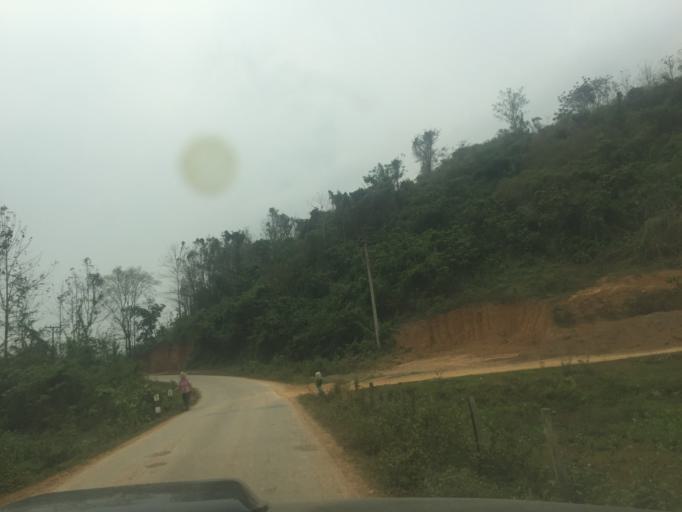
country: LA
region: Vientiane
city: Muang Sanakham
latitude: 18.3982
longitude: 101.5186
